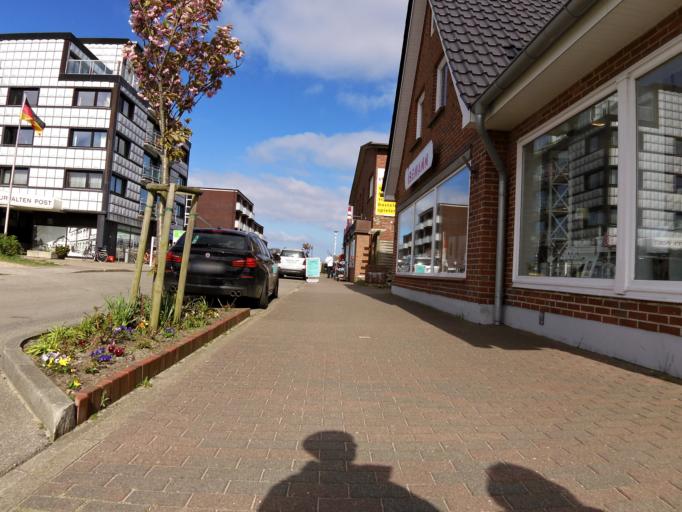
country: DE
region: Schleswig-Holstein
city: Wittdun
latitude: 54.6268
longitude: 8.3971
